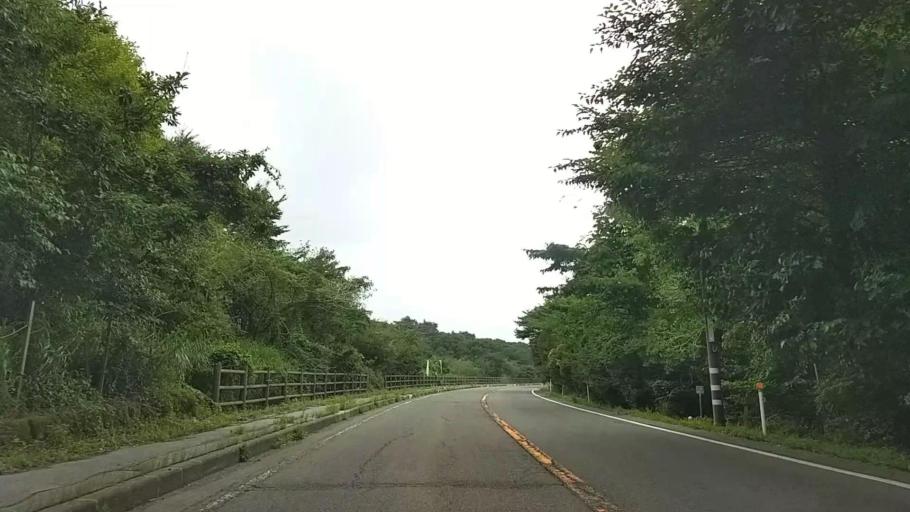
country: JP
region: Yamanashi
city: Fujikawaguchiko
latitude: 35.4381
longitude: 138.6019
